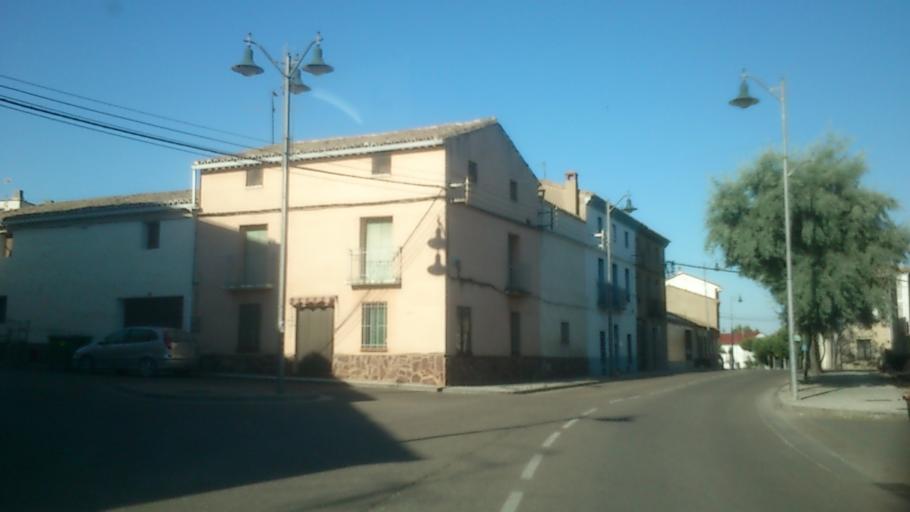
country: ES
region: Aragon
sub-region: Provincia de Zaragoza
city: San Mateo de Gallego
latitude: 41.8294
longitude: -0.7689
